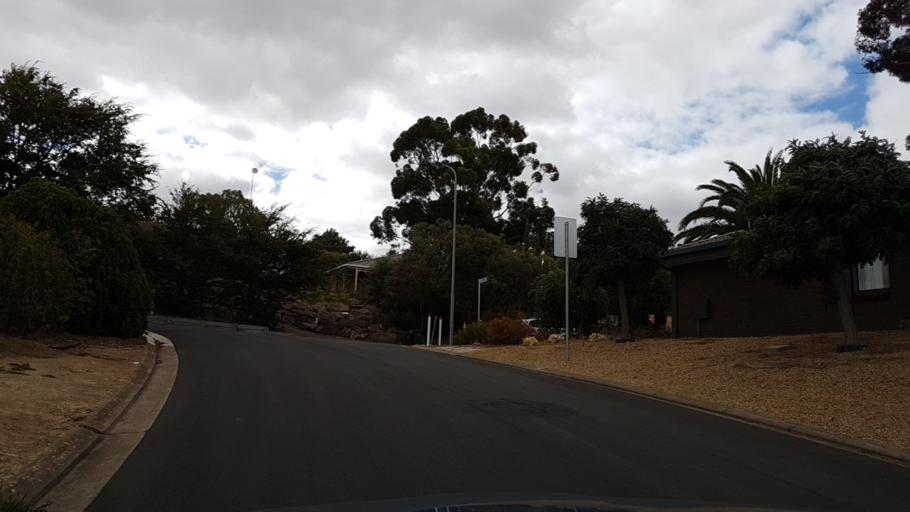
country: AU
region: South Australia
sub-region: Gawler
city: Gawler
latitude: -34.6060
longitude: 138.7592
